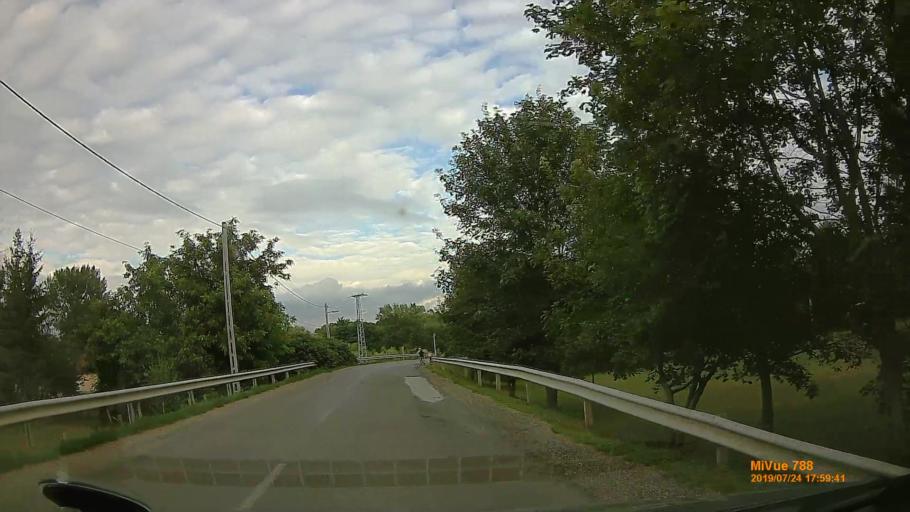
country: HU
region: Borsod-Abauj-Zemplen
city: Encs
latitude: 48.3165
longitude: 21.1593
